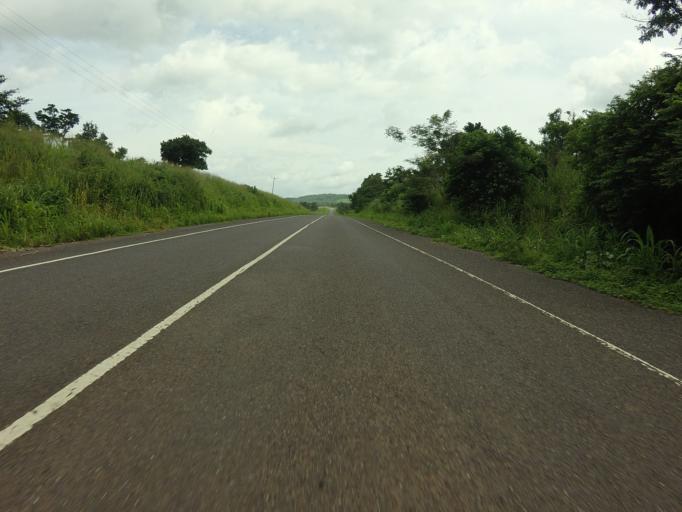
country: TG
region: Plateaux
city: Badou
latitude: 7.9668
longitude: 0.5574
